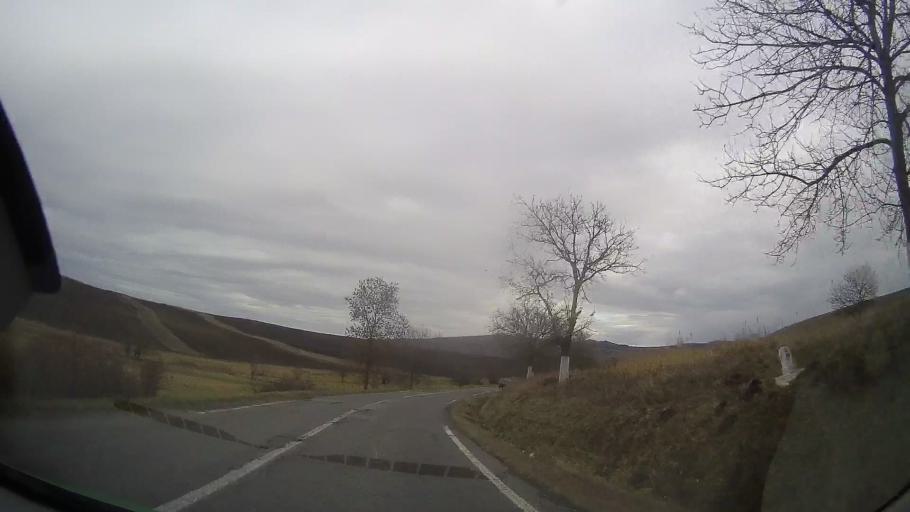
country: RO
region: Mures
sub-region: Comuna Faragau
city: Faragau
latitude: 46.7633
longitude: 24.5438
